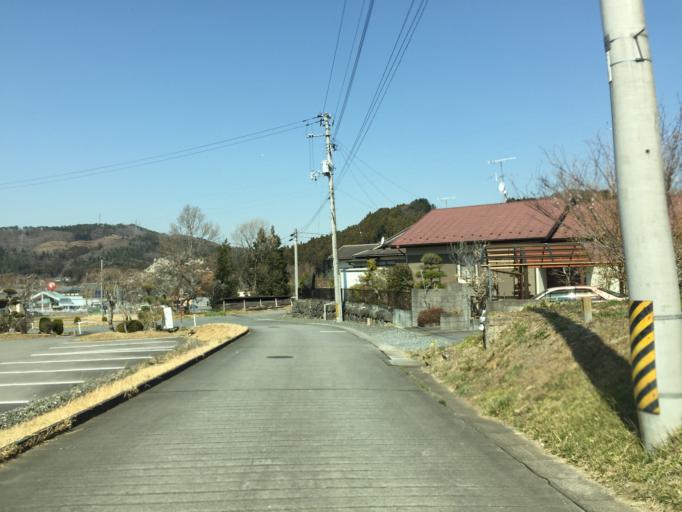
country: JP
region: Fukushima
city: Iwaki
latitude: 37.0049
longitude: 140.7430
